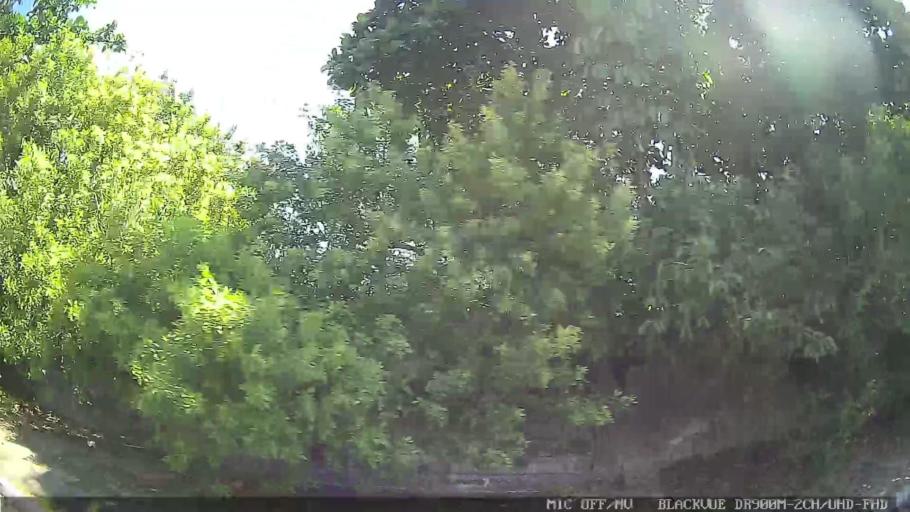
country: BR
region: Sao Paulo
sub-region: Peruibe
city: Peruibe
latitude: -24.3293
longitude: -47.0035
